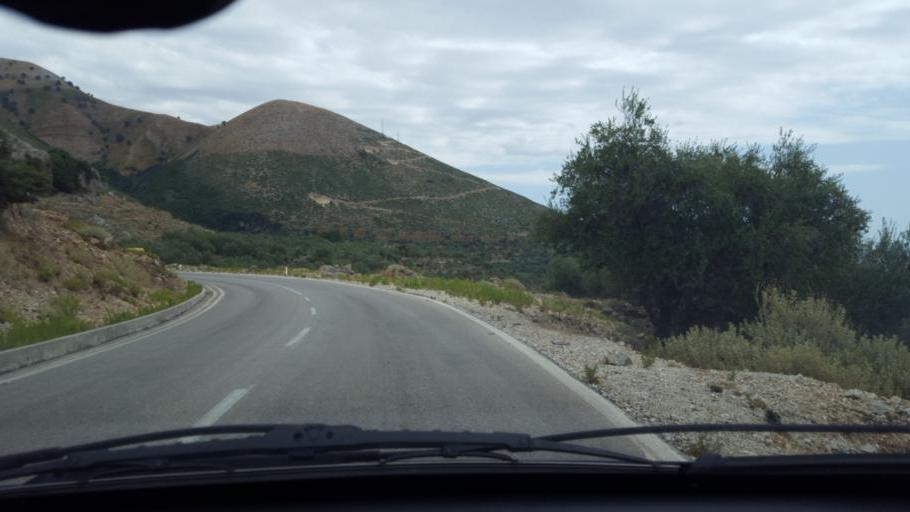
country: AL
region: Vlore
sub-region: Rrethi i Sarandes
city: Lukove
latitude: 40.0368
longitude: 19.8807
